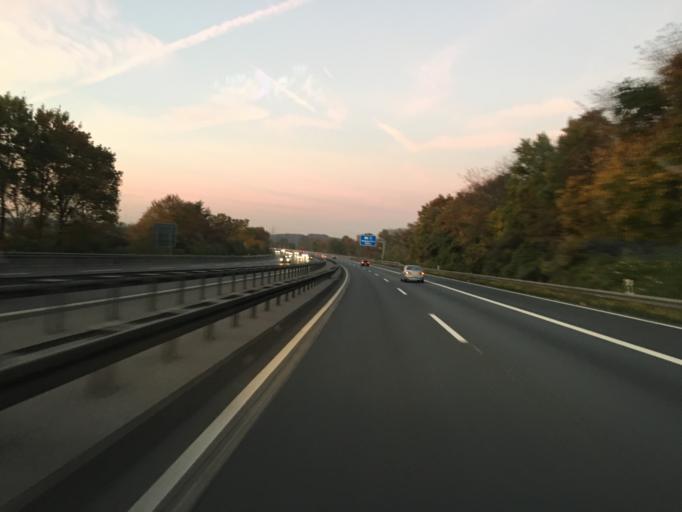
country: DE
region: North Rhine-Westphalia
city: Schwerte
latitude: 51.4109
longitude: 7.5507
